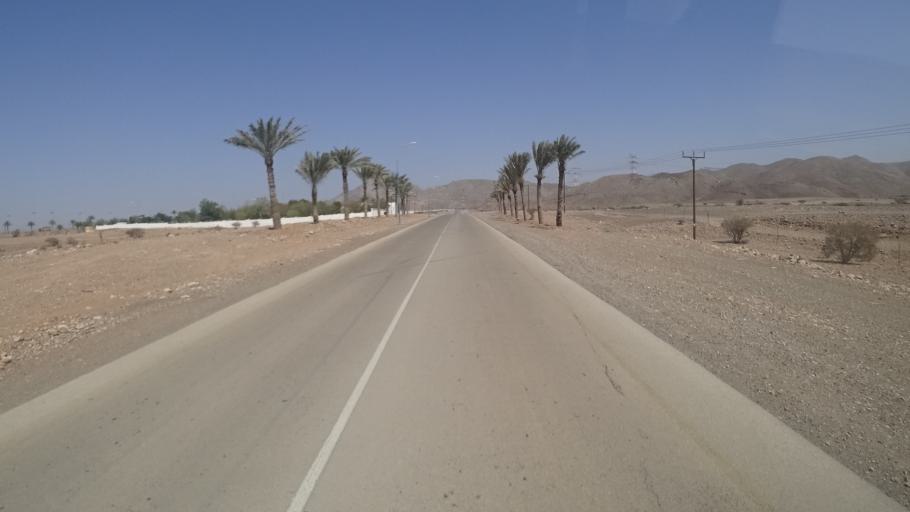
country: OM
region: Ash Sharqiyah
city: Badiyah
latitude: 22.5108
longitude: 58.9478
